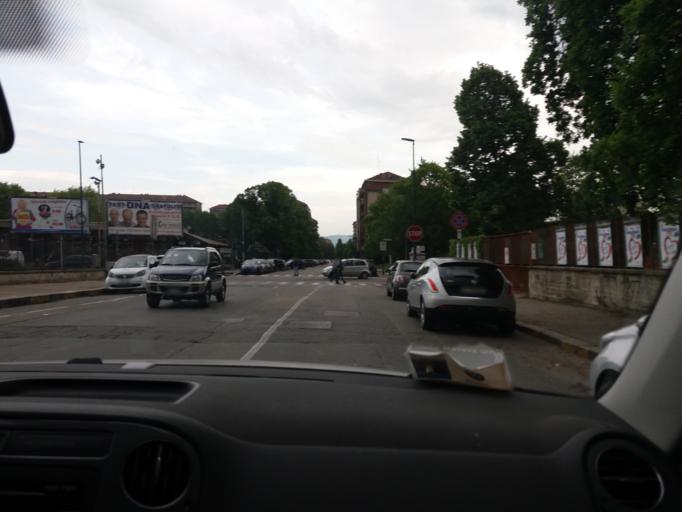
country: IT
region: Piedmont
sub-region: Provincia di Torino
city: Lesna
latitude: 45.0686
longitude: 7.6270
